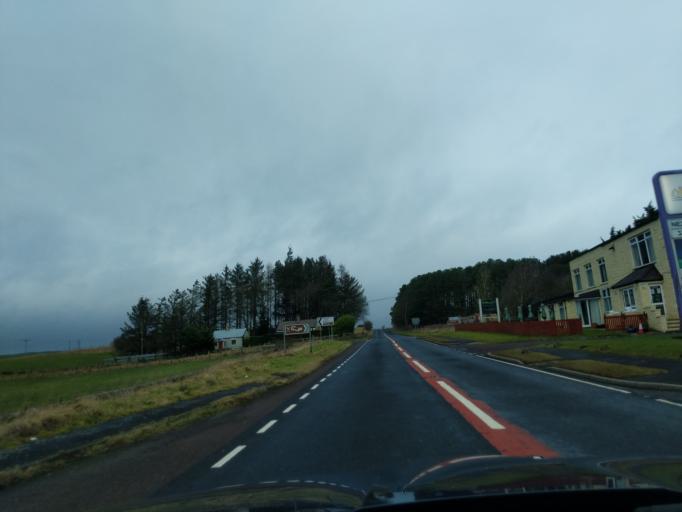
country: GB
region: England
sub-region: Northumberland
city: Rothley
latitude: 55.1652
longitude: -2.0190
